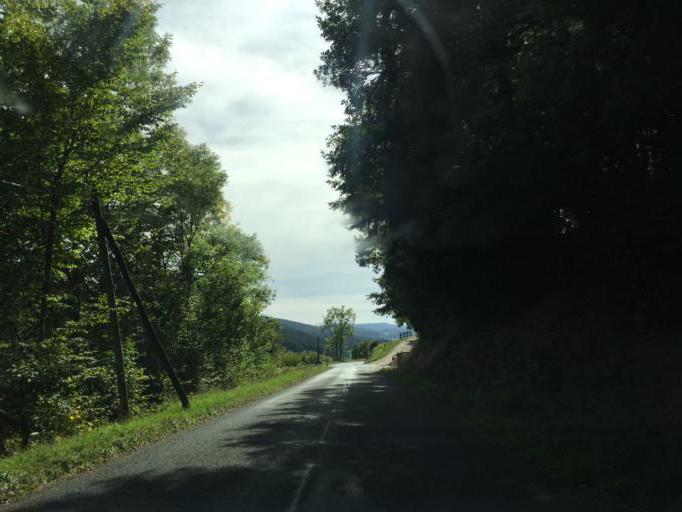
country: FR
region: Rhone-Alpes
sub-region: Departement du Rhone
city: Grandris
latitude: 46.0921
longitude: 4.4339
